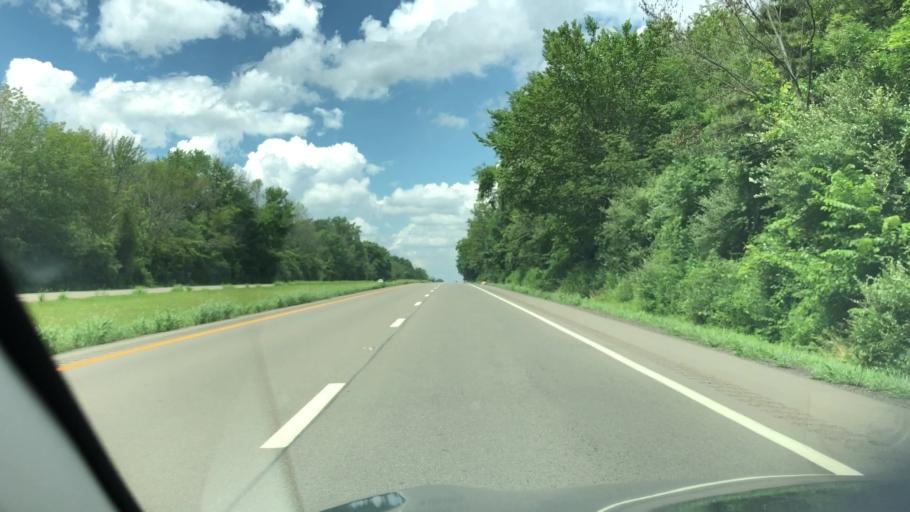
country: US
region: Ohio
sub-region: Stark County
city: Massillon
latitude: 40.8256
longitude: -81.5394
